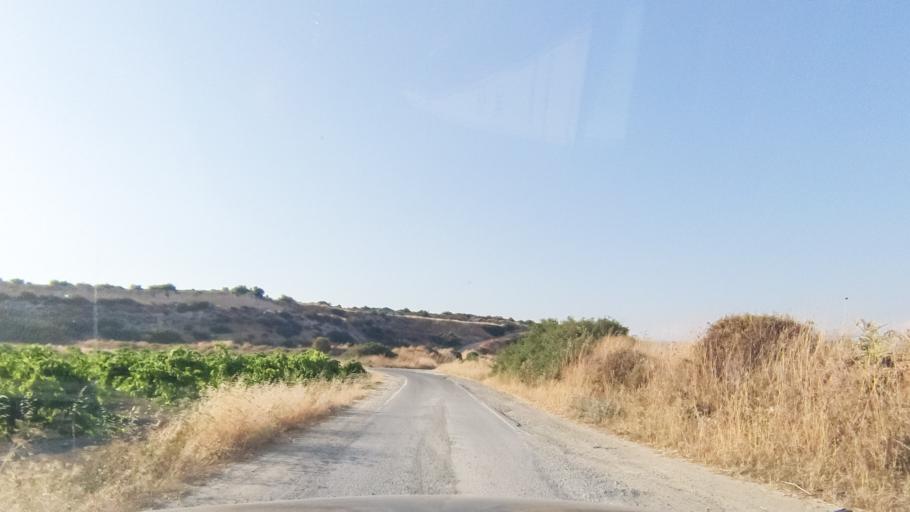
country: CY
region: Limassol
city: Pissouri
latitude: 34.6732
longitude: 32.7668
